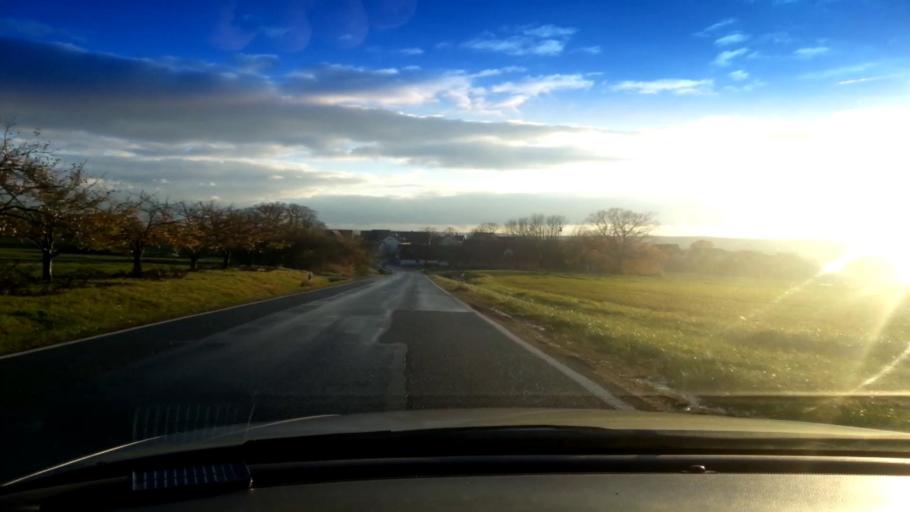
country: DE
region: Bavaria
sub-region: Upper Franconia
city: Buttenheim
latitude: 49.8304
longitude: 11.0294
